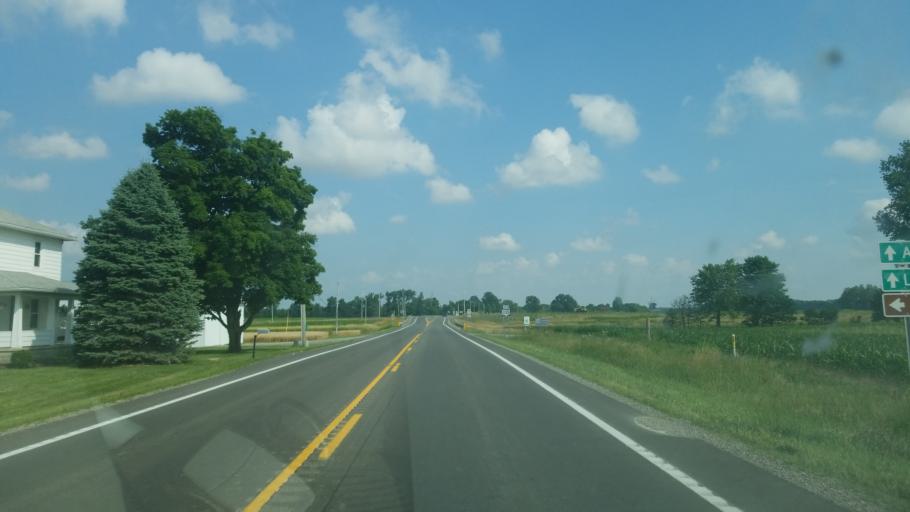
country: US
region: Ohio
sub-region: Logan County
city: Russells Point
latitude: 40.5296
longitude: -83.8310
